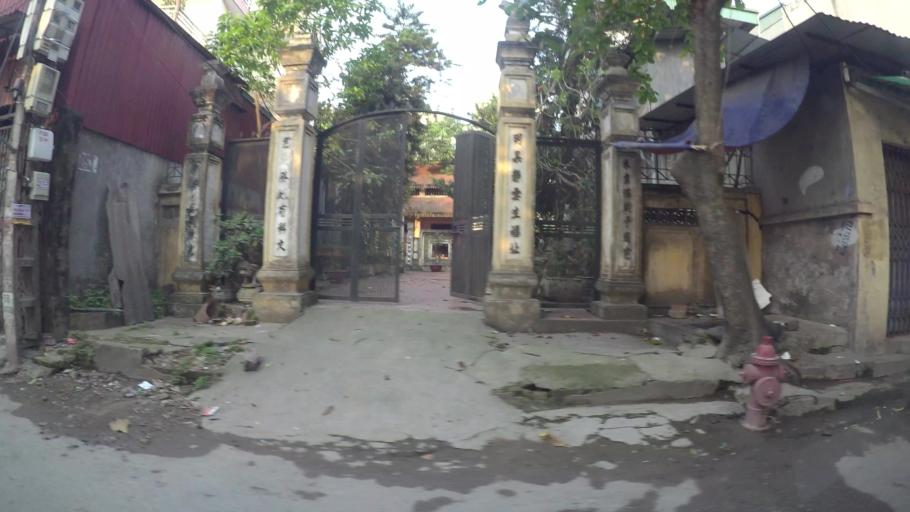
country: VN
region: Ha Noi
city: Tay Ho
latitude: 21.0687
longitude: 105.7918
